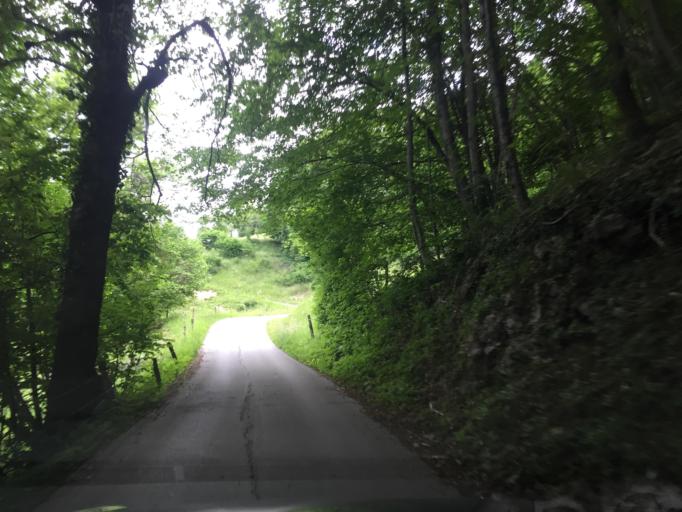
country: SI
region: Tolmin
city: Tolmin
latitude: 46.1641
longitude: 13.8375
